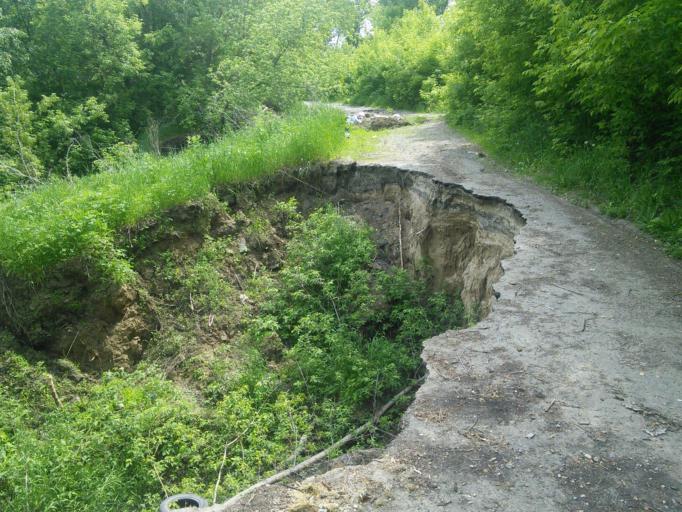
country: RU
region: Altai Krai
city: Sannikovo
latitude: 53.3589
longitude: 84.0032
